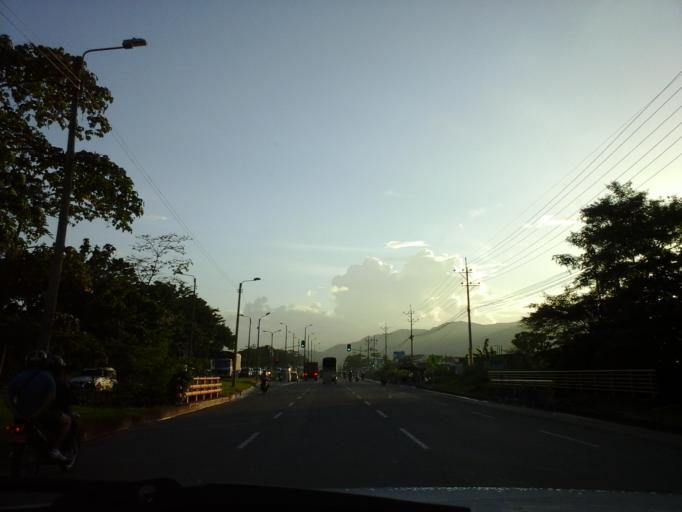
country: CO
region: Meta
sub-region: Villavicencio
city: Villavicencio
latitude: 4.1182
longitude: -73.6213
